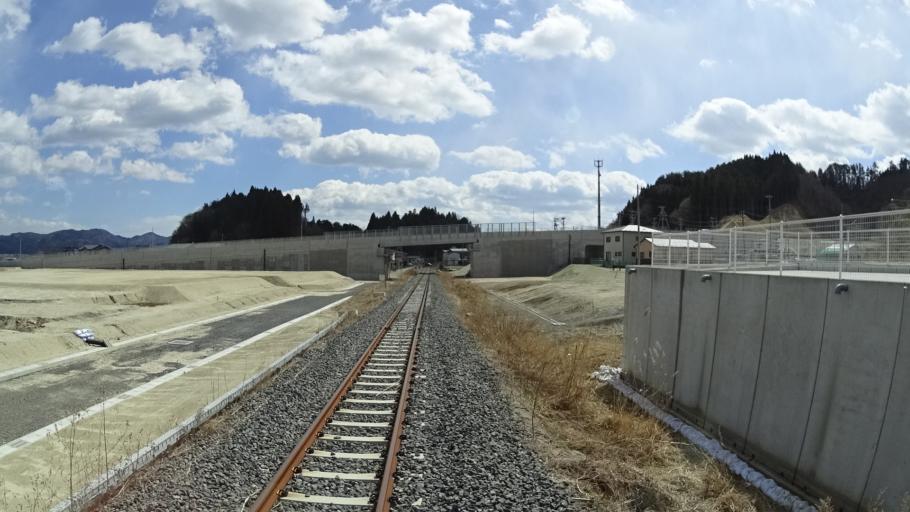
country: JP
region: Iwate
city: Yamada
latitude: 39.4738
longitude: 141.9475
